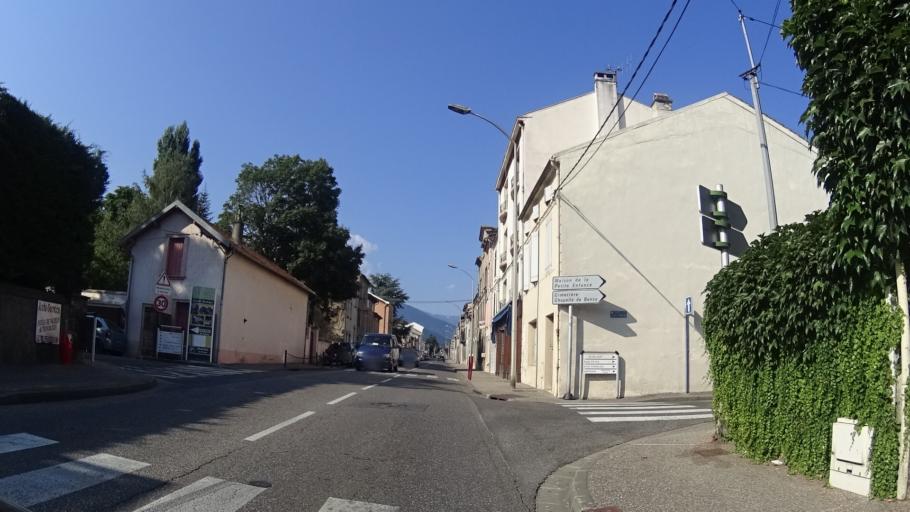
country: FR
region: Midi-Pyrenees
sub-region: Departement de l'Ariege
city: Lavelanet
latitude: 42.9305
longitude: 1.8450
